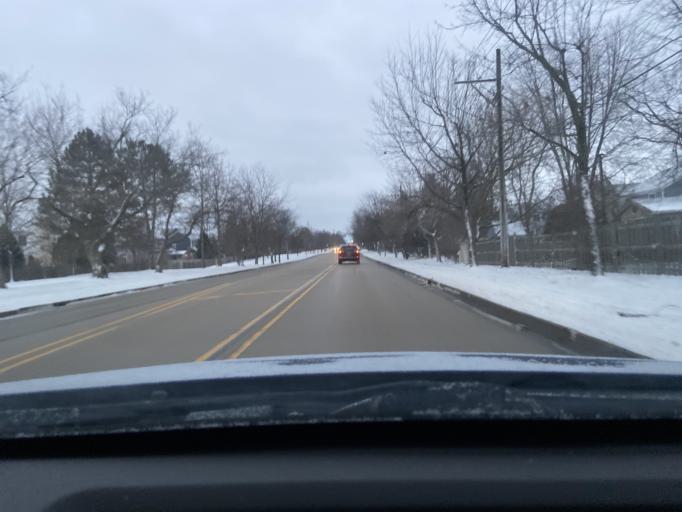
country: US
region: Illinois
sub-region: Lake County
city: Grayslake
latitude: 42.3498
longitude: -88.0241
